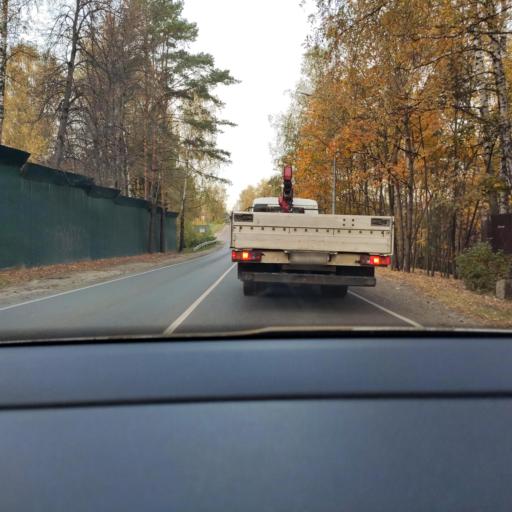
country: RU
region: Moskovskaya
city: Cherkizovo
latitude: 55.9713
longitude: 37.7708
